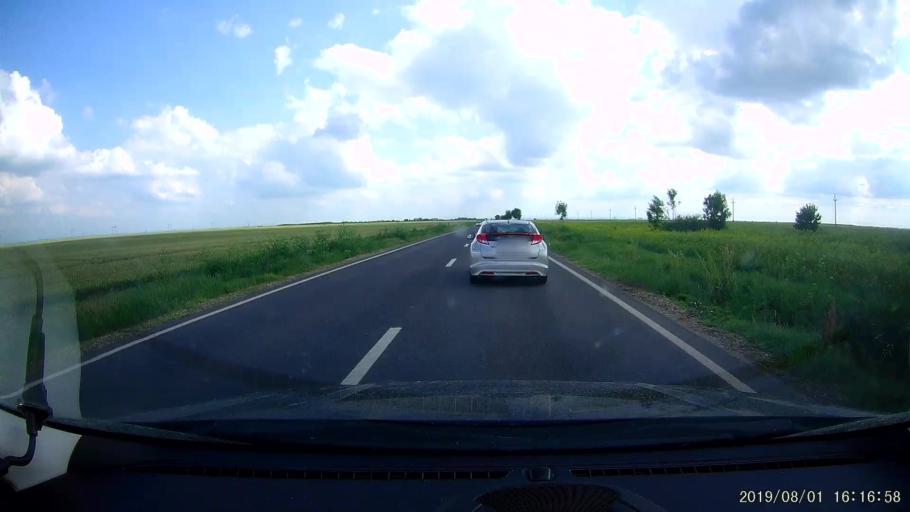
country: RO
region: Calarasi
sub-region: Comuna Stefan Voda
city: Stefan Voda
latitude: 44.3116
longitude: 27.3565
